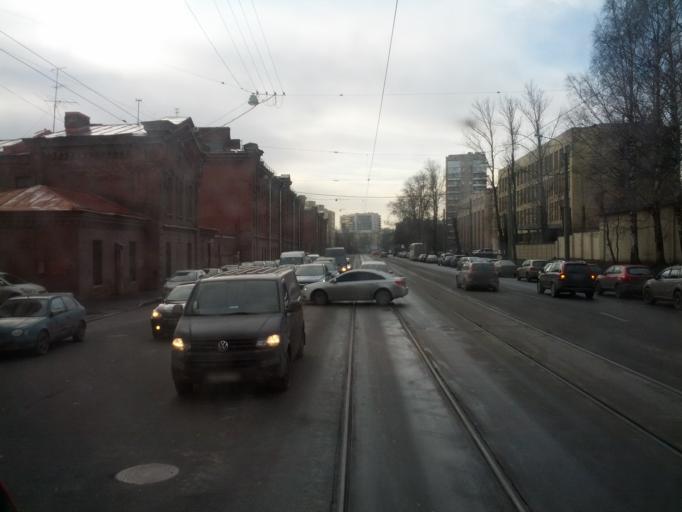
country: RU
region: St.-Petersburg
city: Centralniy
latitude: 59.9404
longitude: 30.4086
